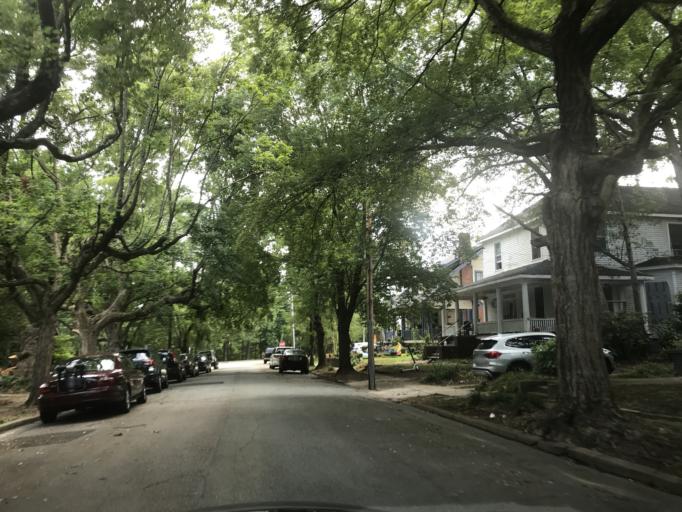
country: US
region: North Carolina
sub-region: Wake County
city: Raleigh
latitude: 35.7753
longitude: -78.6497
